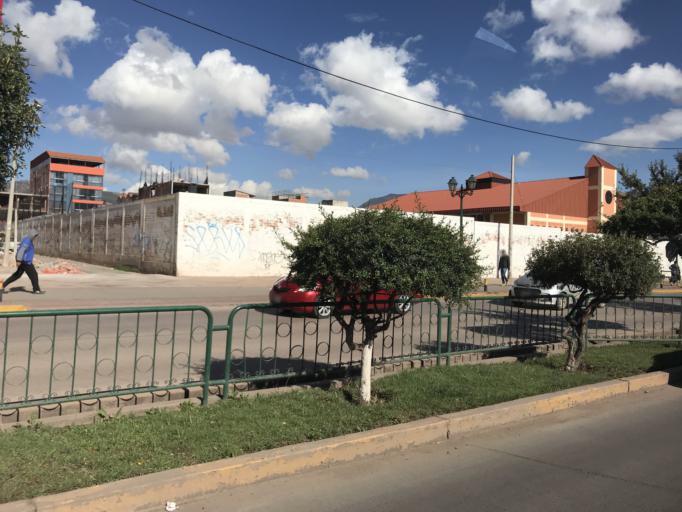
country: PE
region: Cusco
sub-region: Provincia de Cusco
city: Cusco
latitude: -13.5354
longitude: -71.9556
